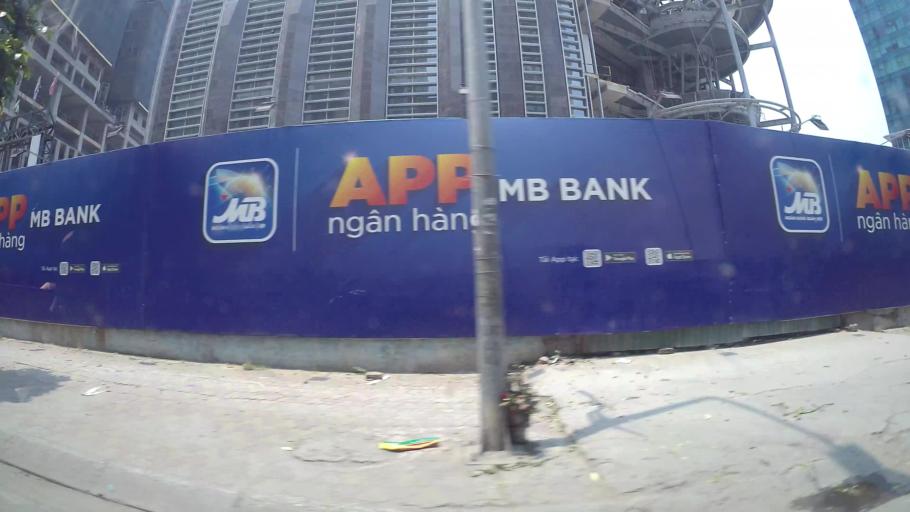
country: VN
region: Ha Noi
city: Thanh Xuan
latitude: 21.0074
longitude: 105.8075
